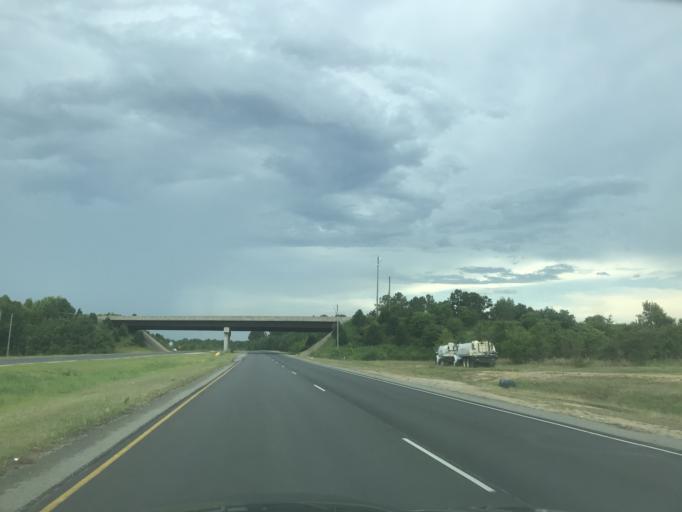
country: US
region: North Carolina
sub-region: Johnston County
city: Clayton
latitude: 35.6048
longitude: -78.4159
